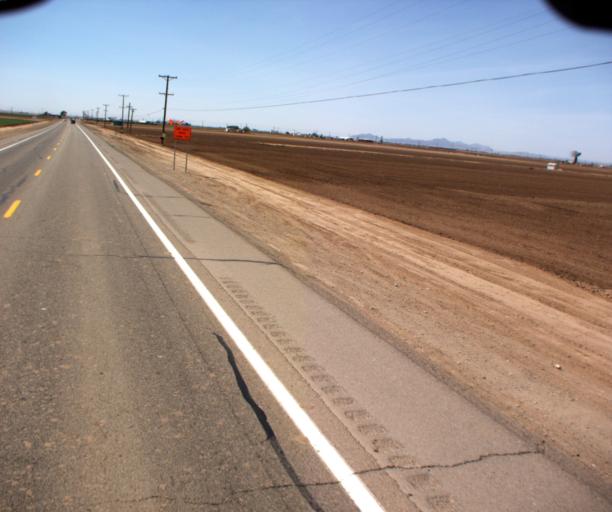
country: US
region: Arizona
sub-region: Yuma County
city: Fortuna Foothills
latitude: 32.6997
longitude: -114.4530
